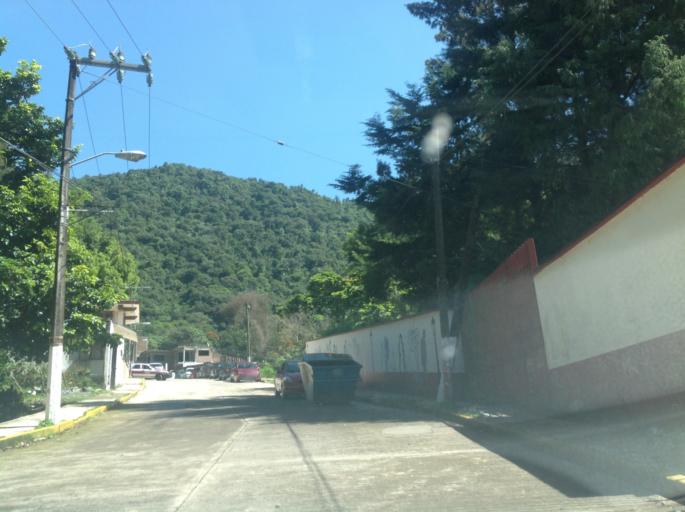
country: MX
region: Veracruz
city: Nogales
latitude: 18.8448
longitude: -97.1606
